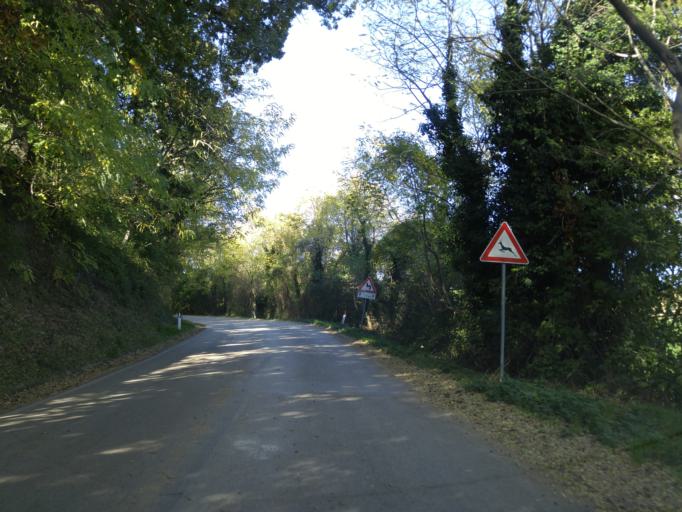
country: IT
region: The Marches
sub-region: Provincia di Pesaro e Urbino
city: Serrungarina
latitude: 43.7503
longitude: 12.8663
